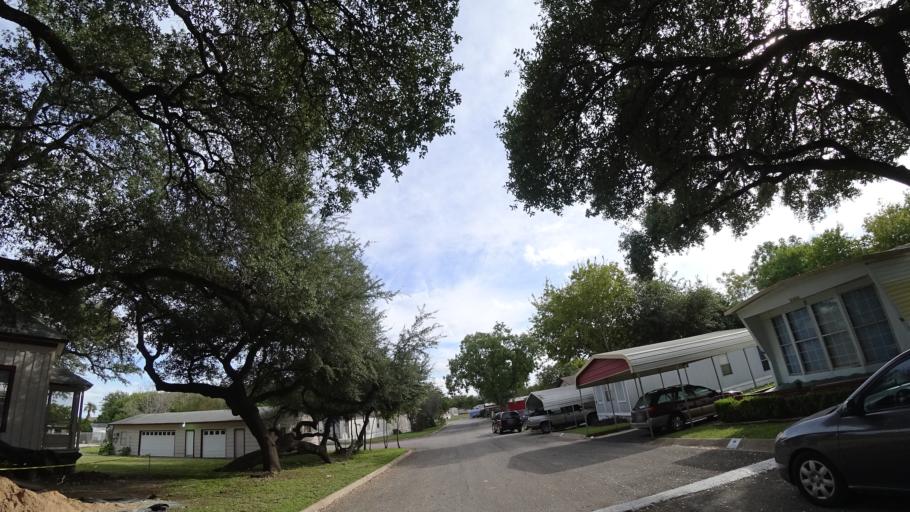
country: US
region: Texas
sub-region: Travis County
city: Onion Creek
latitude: 30.1993
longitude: -97.7577
